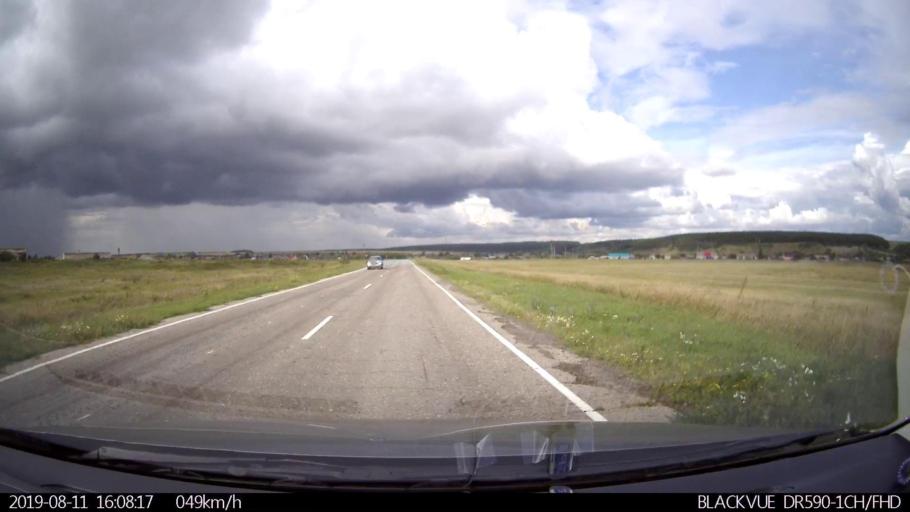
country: RU
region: Ulyanovsk
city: Ignatovka
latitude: 53.9833
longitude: 47.6486
